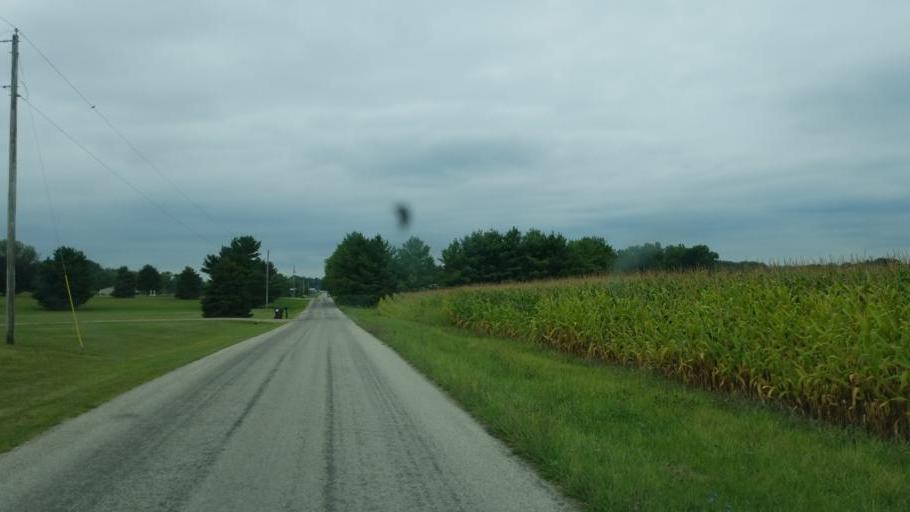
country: US
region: Ohio
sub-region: Morrow County
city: Mount Gilead
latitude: 40.5172
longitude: -82.8045
